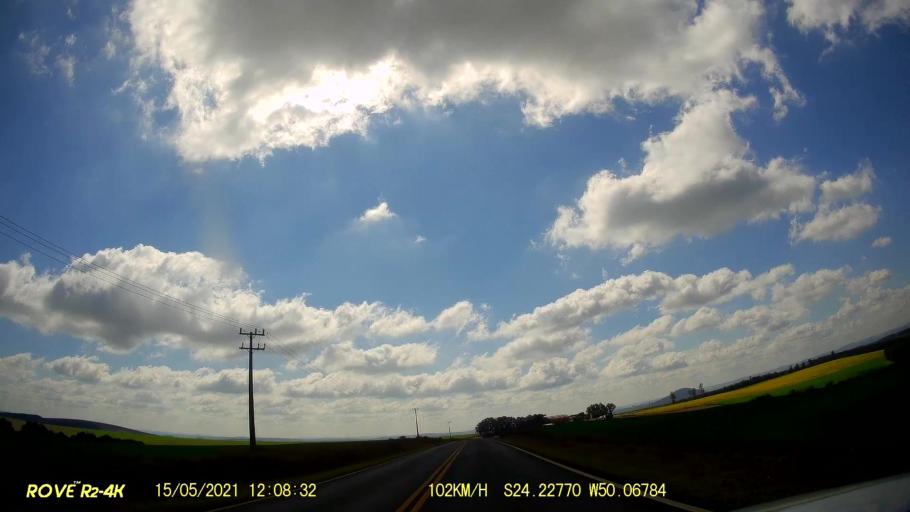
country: BR
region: Parana
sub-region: Pirai Do Sul
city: Pirai do Sul
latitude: -24.2278
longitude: -50.0676
